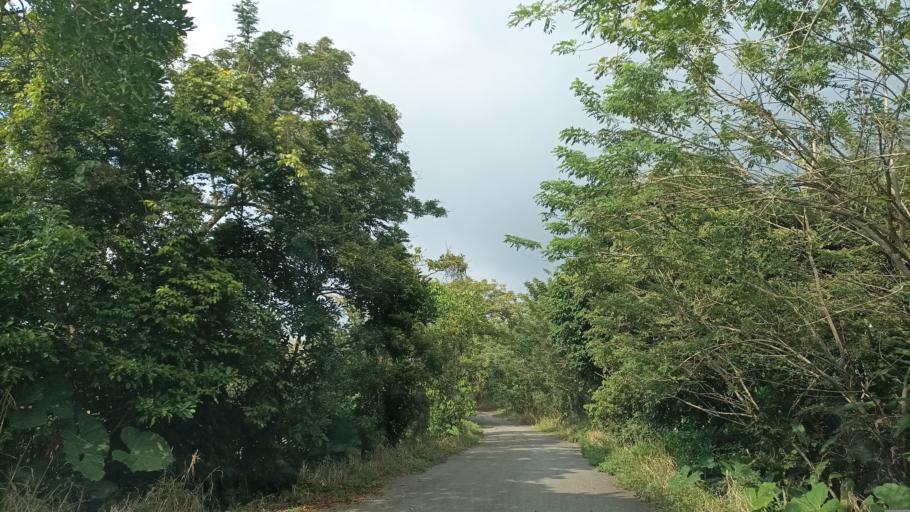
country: MX
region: Veracruz
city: Allende
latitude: 18.1029
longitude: -94.2941
